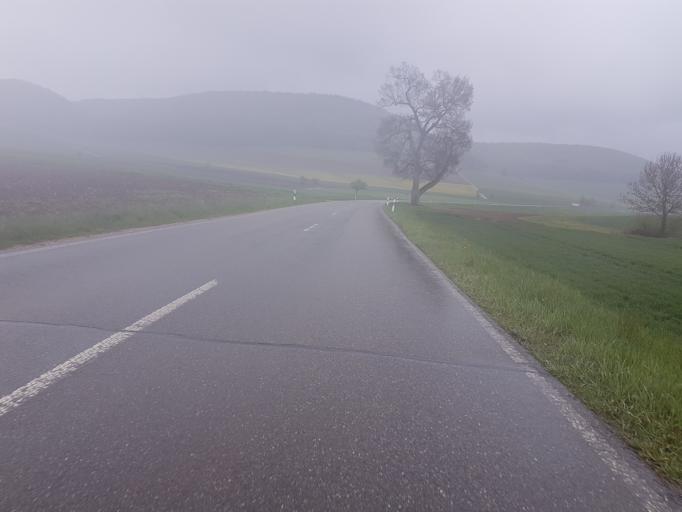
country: DE
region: Baden-Wuerttemberg
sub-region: Freiburg Region
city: Blumberg
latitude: 47.8838
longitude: 8.5592
